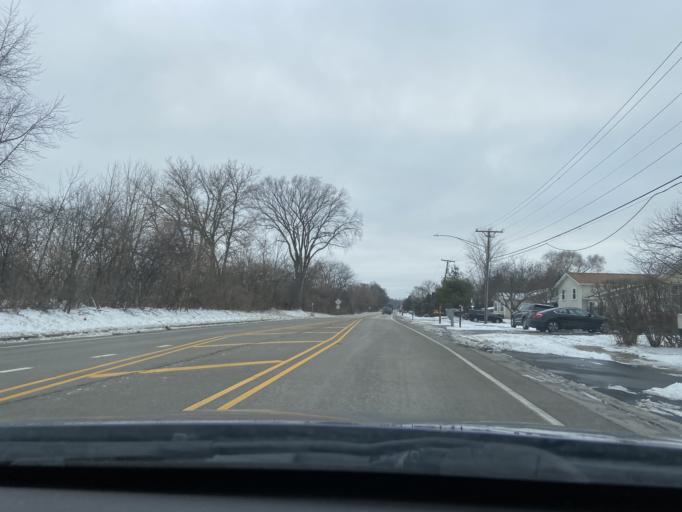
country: US
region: Illinois
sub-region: Lake County
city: Round Lake Park
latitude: 42.3775
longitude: -88.0642
